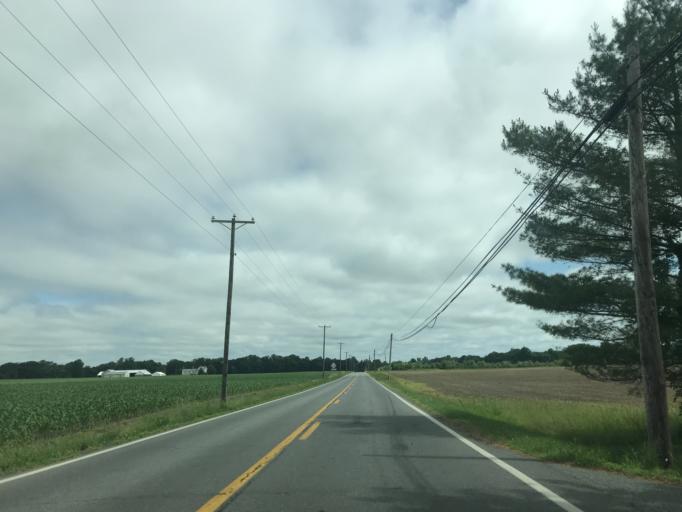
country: US
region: Maryland
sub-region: Caroline County
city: Ridgely
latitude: 38.9074
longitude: -75.9580
